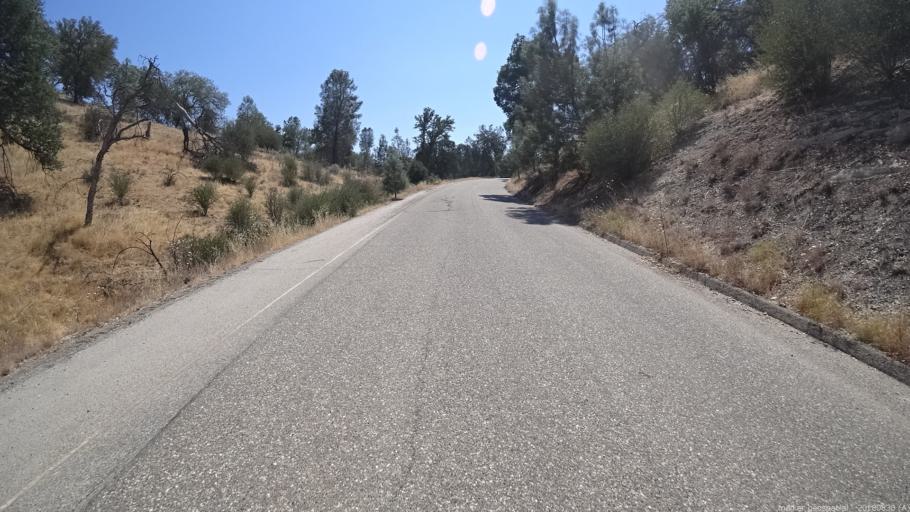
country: US
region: California
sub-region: Monterey County
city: King City
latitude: 35.9947
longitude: -121.2623
